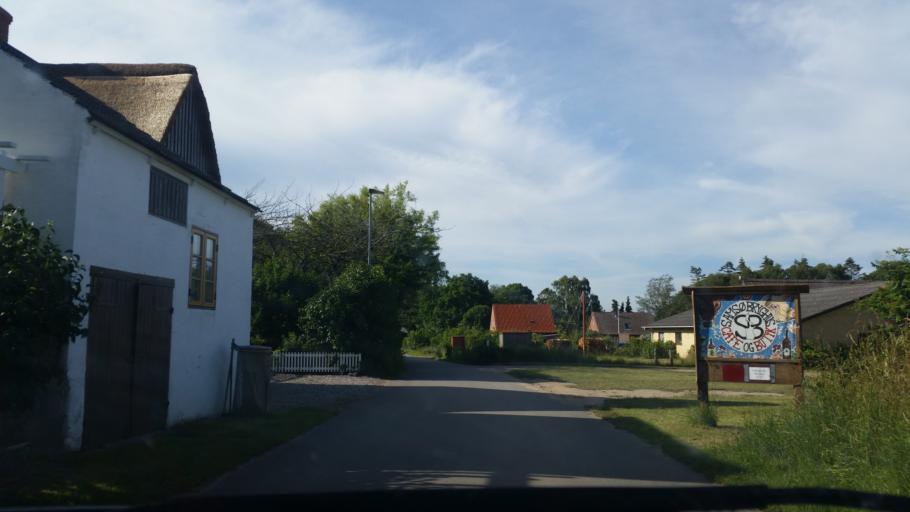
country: DK
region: Central Jutland
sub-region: Samso Kommune
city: Tranebjerg
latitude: 55.9648
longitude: 10.5556
